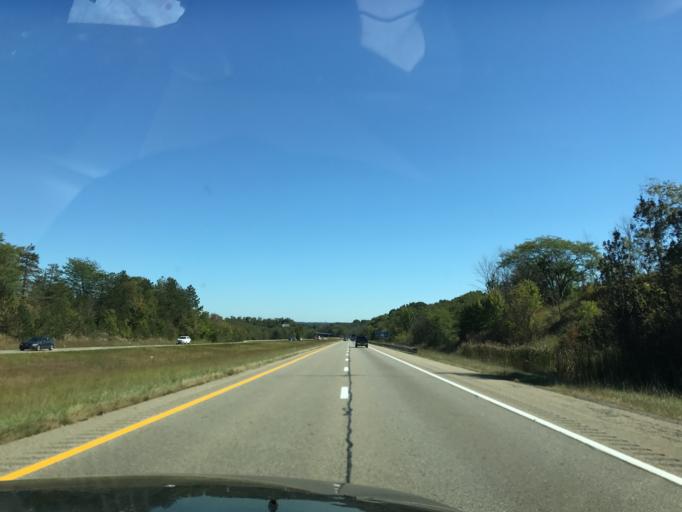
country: US
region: Ohio
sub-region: Muskingum County
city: Zanesville
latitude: 39.9449
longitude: -82.0808
